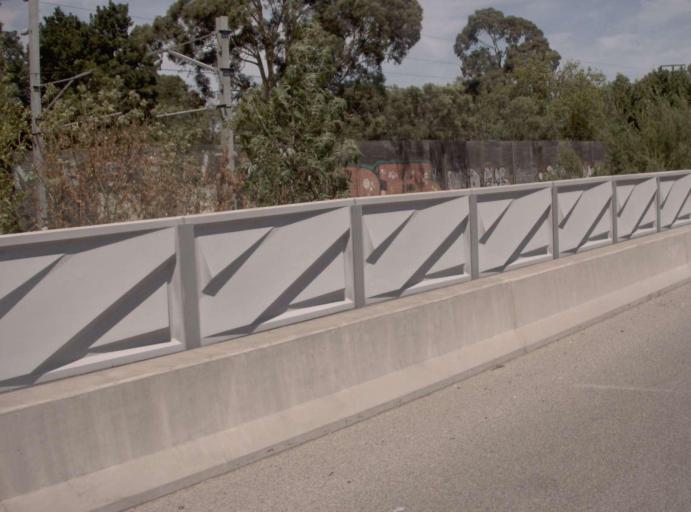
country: AU
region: Victoria
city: Carnegie
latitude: -37.8771
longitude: 145.0750
